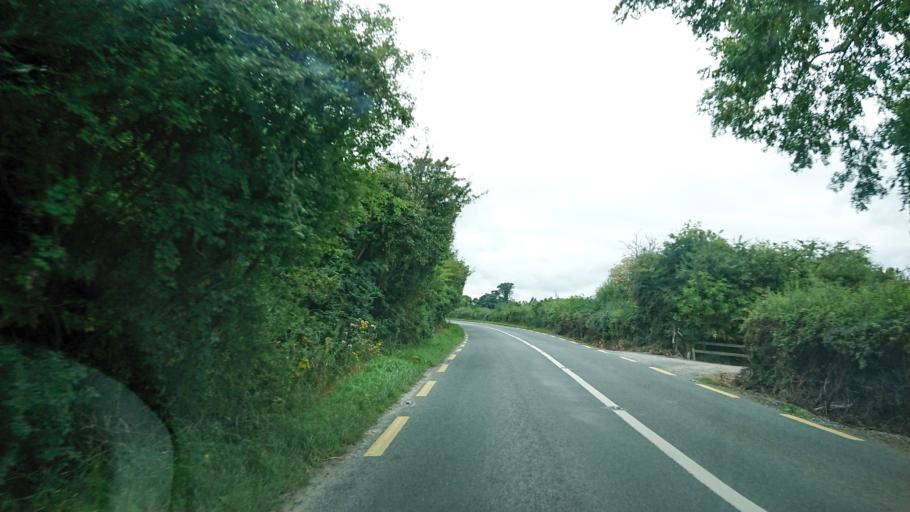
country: IE
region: Munster
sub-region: County Cork
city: Mallow
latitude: 52.1525
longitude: -8.5952
